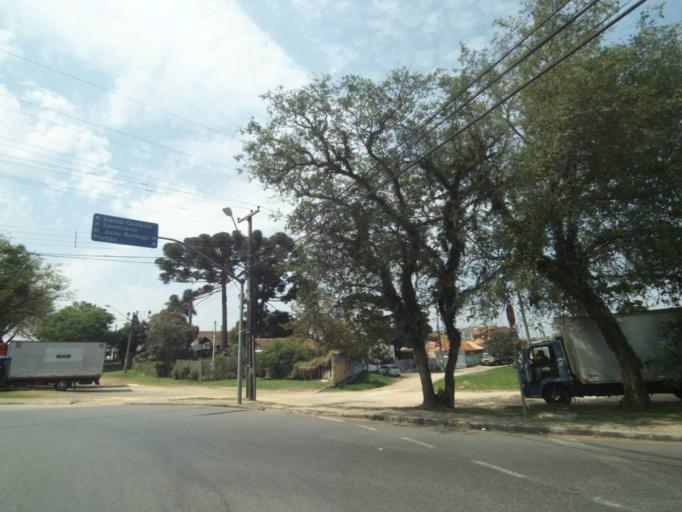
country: BR
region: Parana
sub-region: Curitiba
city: Curitiba
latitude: -25.4754
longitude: -49.3184
